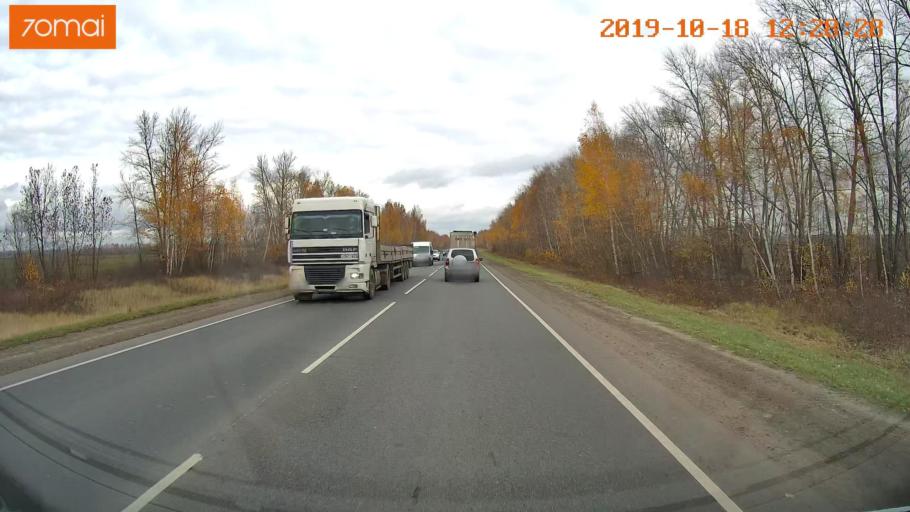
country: RU
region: Rjazan
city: Ryazan'
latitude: 54.5722
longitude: 39.5690
